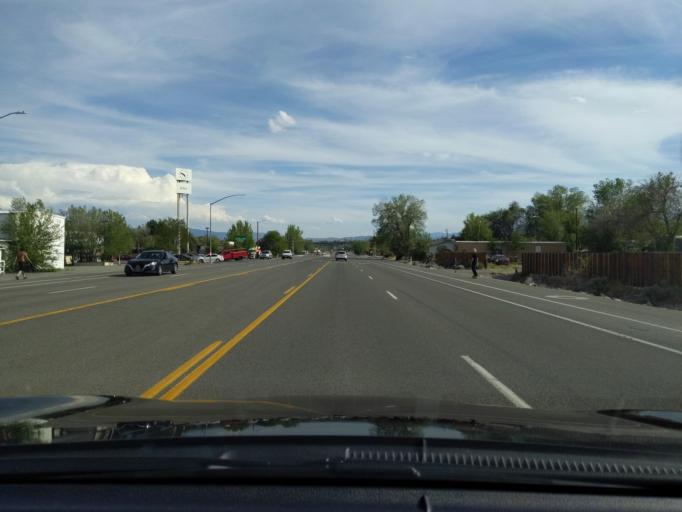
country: US
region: Nevada
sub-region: Washoe County
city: Sun Valley
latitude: 39.5878
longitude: -119.7805
